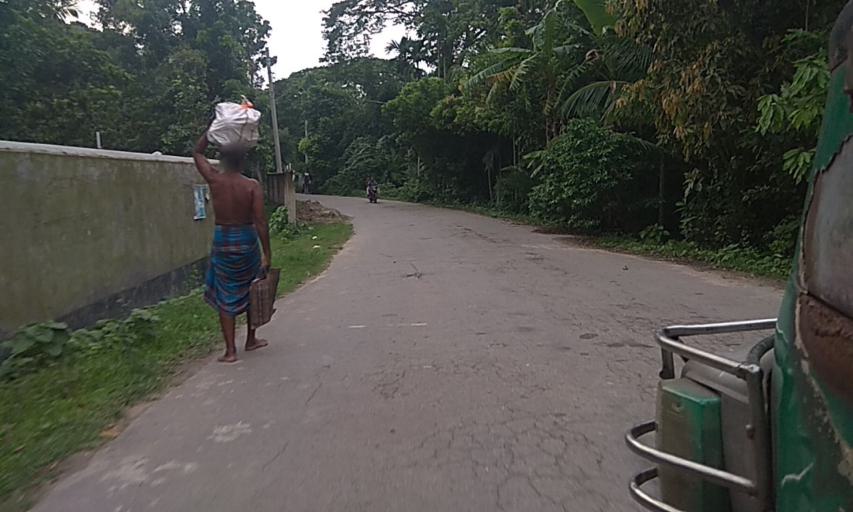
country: BD
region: Dhaka
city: Dohar
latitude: 23.4568
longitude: 90.0023
